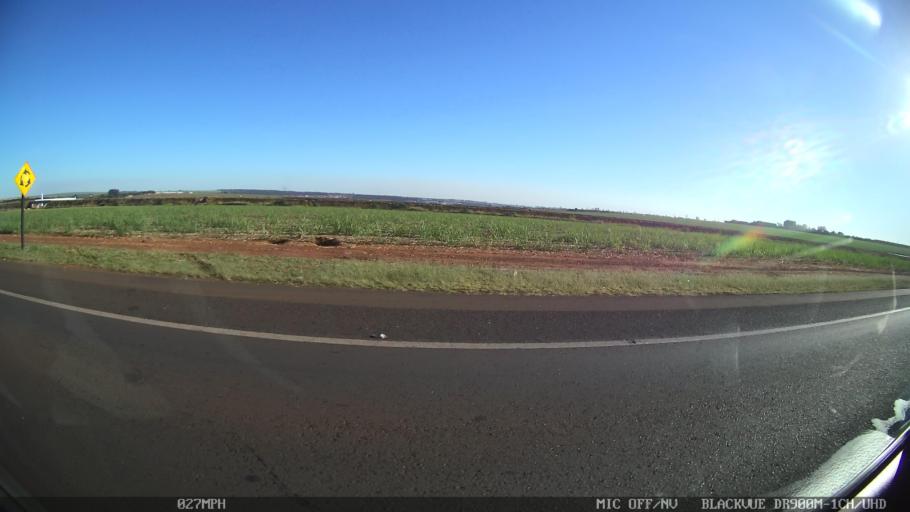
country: BR
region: Sao Paulo
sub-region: Americo Brasiliense
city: Americo Brasiliense
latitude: -21.7714
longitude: -48.1050
